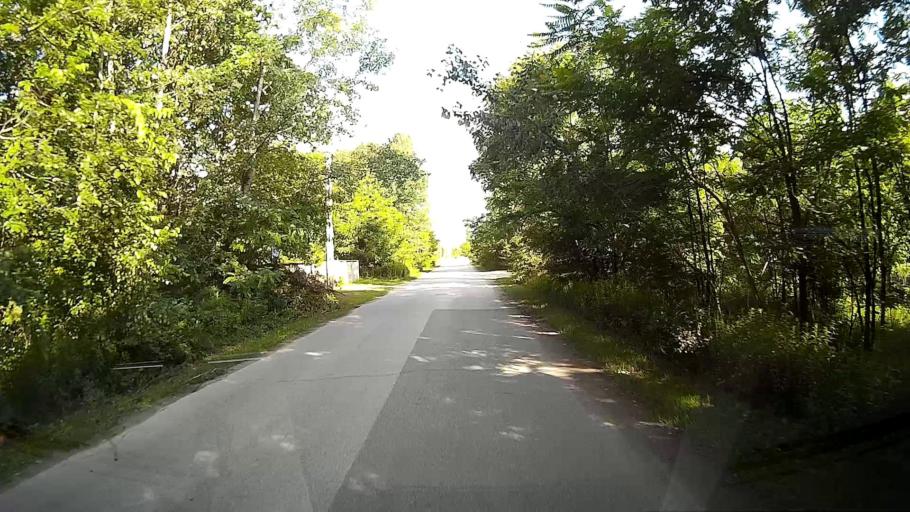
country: HU
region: Pest
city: God
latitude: 47.6808
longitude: 19.1118
